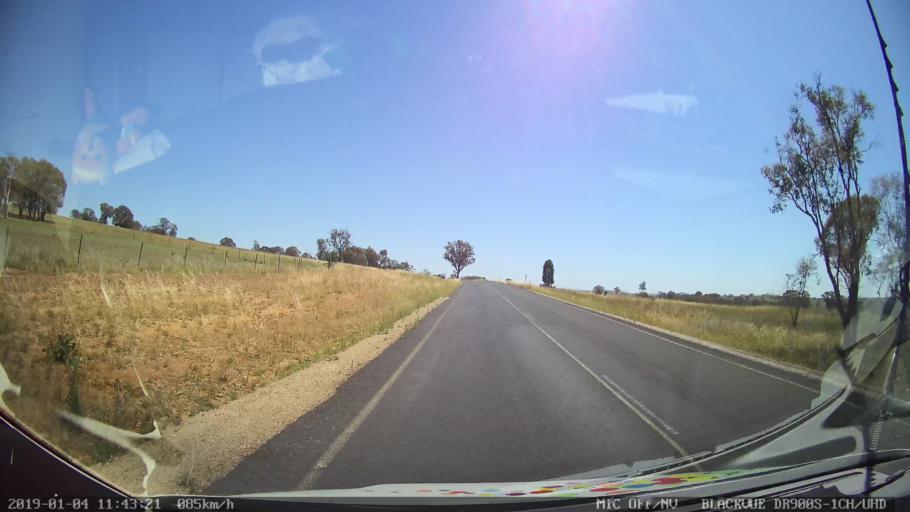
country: AU
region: New South Wales
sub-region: Cabonne
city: Molong
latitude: -32.9701
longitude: 148.7841
